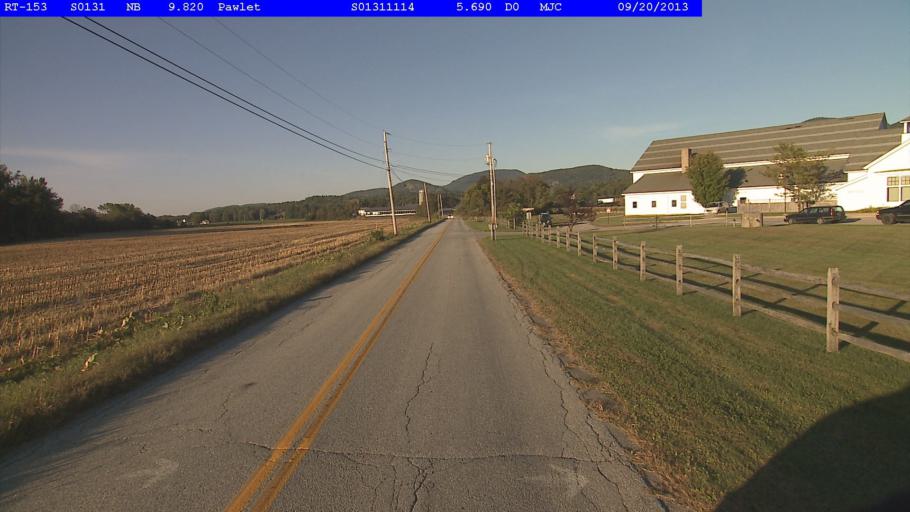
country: US
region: New York
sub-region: Washington County
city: Granville
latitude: 43.3854
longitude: -73.2248
